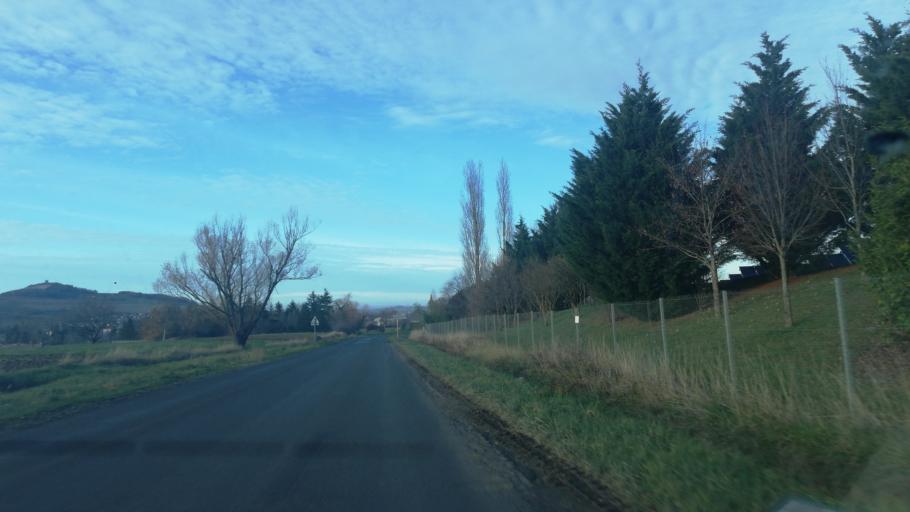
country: FR
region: Auvergne
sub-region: Departement du Puy-de-Dome
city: Billom
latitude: 45.7123
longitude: 3.3481
